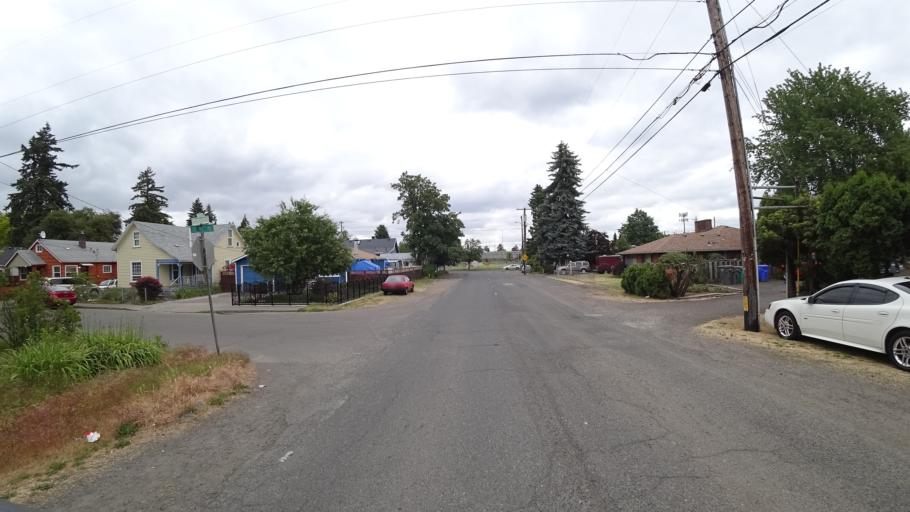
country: US
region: Oregon
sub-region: Multnomah County
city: Lents
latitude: 45.4822
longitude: -122.5698
